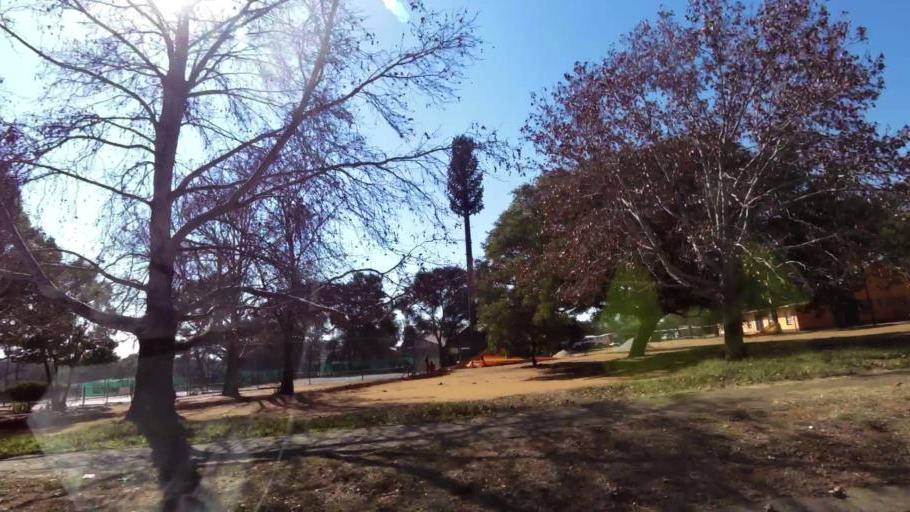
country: ZA
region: Gauteng
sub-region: City of Johannesburg Metropolitan Municipality
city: Roodepoort
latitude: -26.1367
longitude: 27.9516
